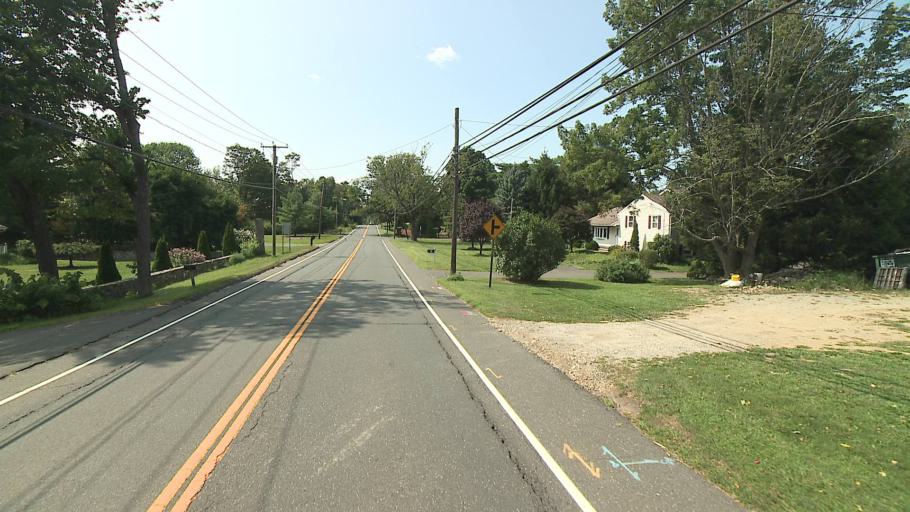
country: US
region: Connecticut
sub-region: Fairfield County
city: Newtown
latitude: 41.4172
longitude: -73.3265
